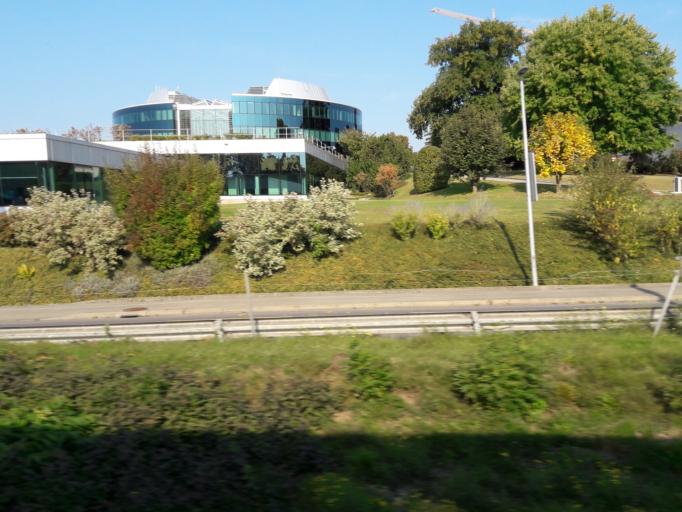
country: CH
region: Vaud
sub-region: Morges District
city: Morges
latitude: 46.5011
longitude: 6.4844
